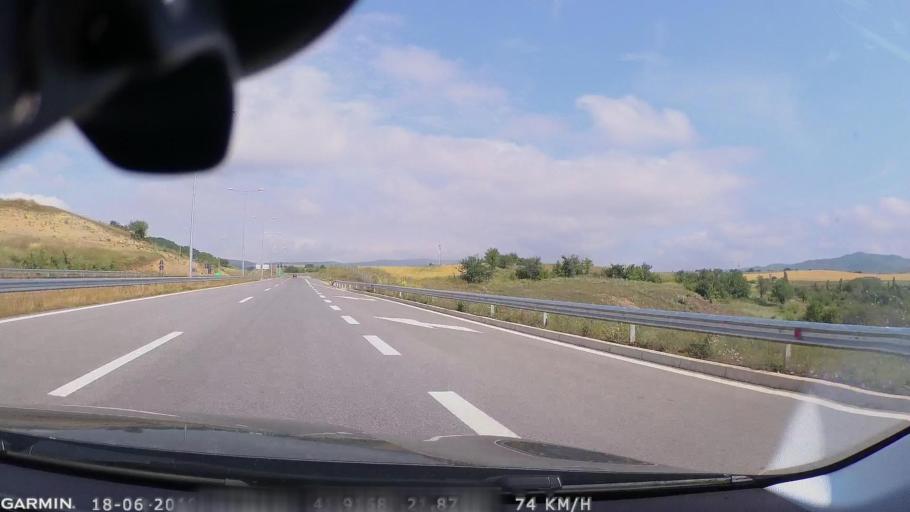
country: MK
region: Sveti Nikole
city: Gorobinci
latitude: 41.9177
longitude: 21.8797
